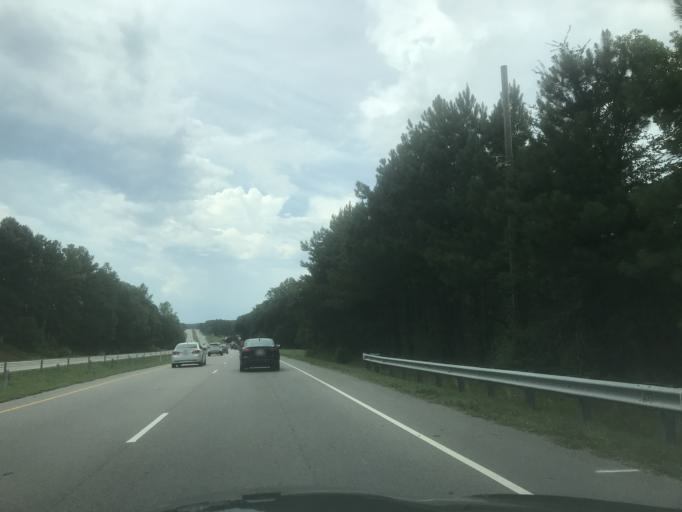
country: US
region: North Carolina
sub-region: Johnston County
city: Clayton
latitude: 35.6821
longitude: -78.5337
